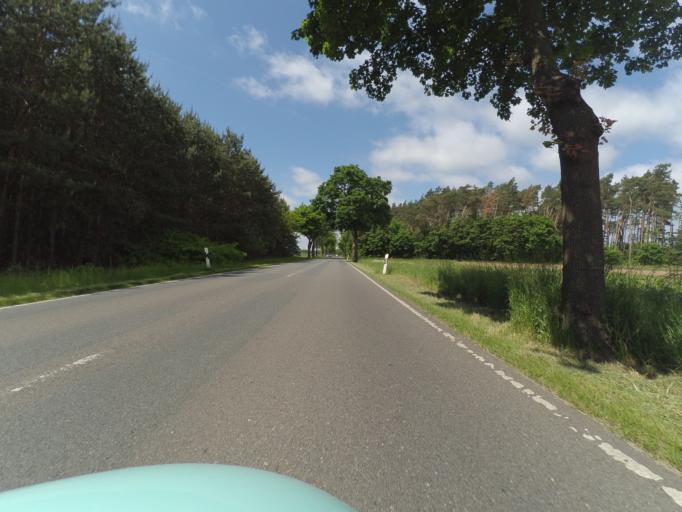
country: DE
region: Lower Saxony
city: Leiferde
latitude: 52.4372
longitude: 10.4620
